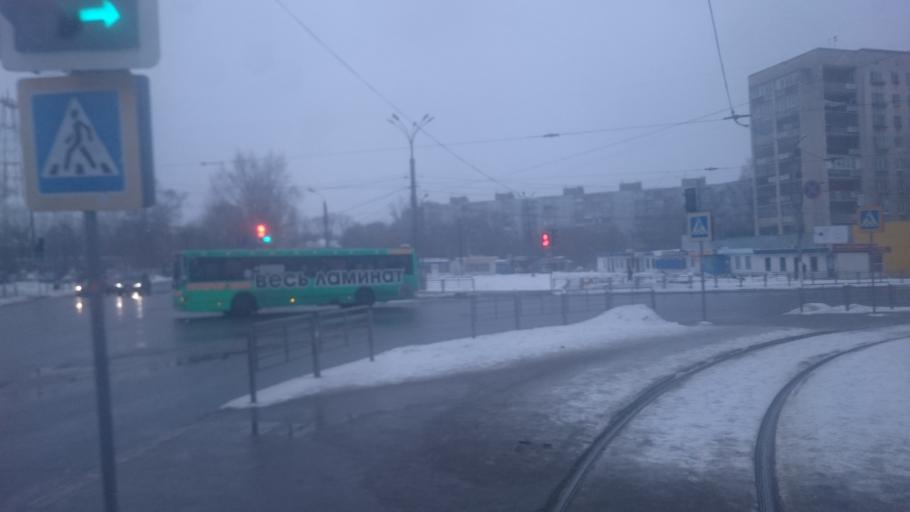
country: RU
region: Tverskaya
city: Tver
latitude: 56.8369
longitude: 35.8939
